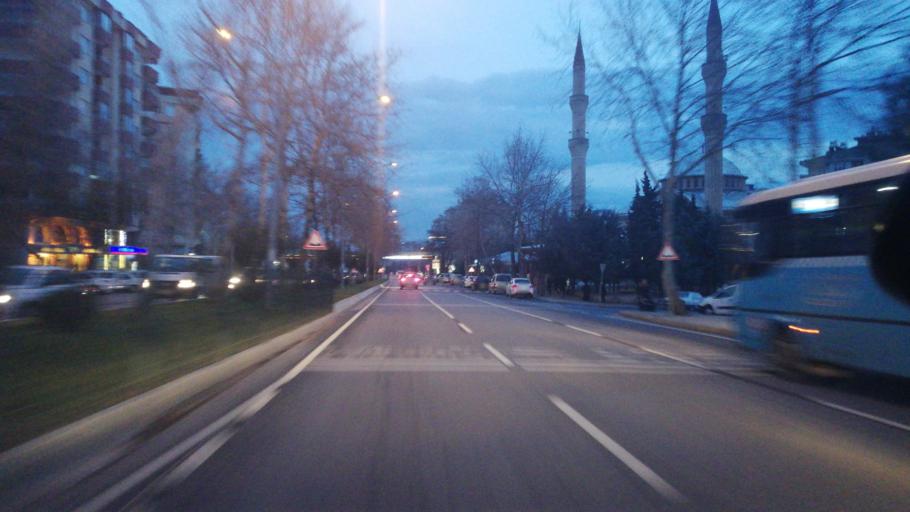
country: TR
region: Kahramanmaras
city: Kahramanmaras
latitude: 37.5861
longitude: 36.8990
